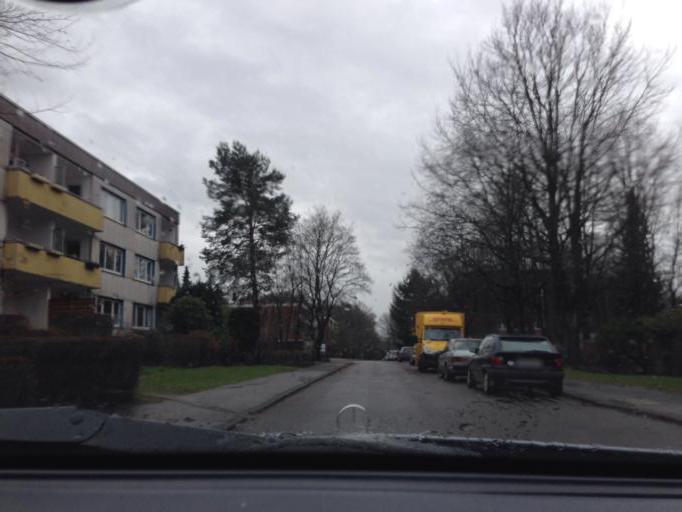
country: DE
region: Schleswig-Holstein
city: Barsbuettel
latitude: 53.5877
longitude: 10.1723
